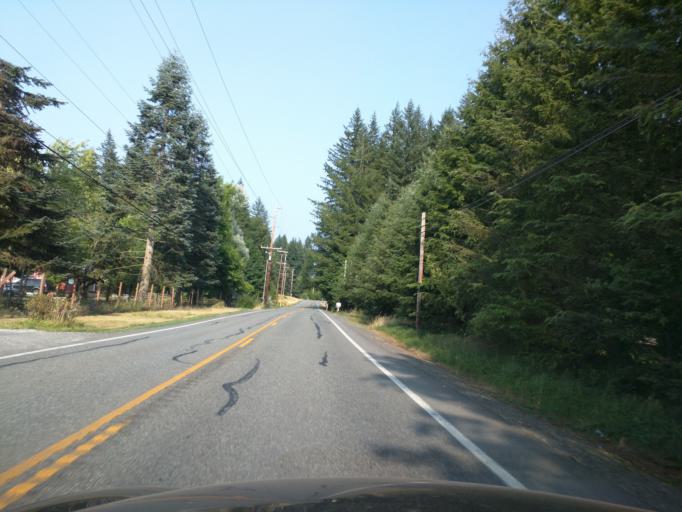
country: US
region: Washington
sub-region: Whatcom County
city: Peaceful Valley
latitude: 48.9172
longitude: -122.1293
